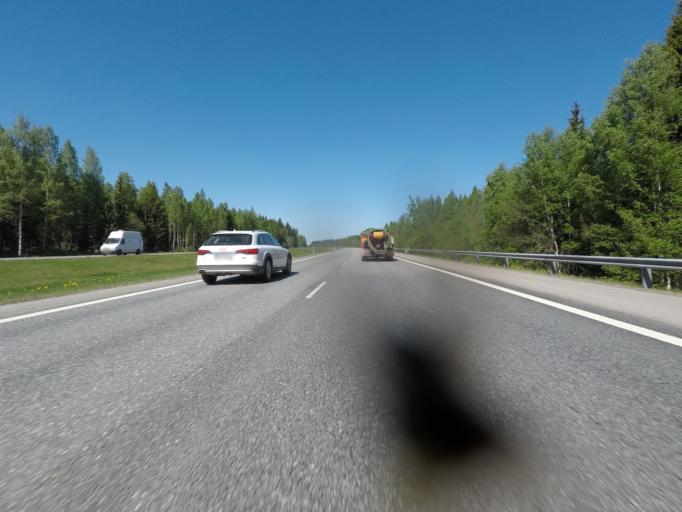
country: FI
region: Haeme
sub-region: Haemeenlinna
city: Haemeenlinna
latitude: 60.9464
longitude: 24.5073
